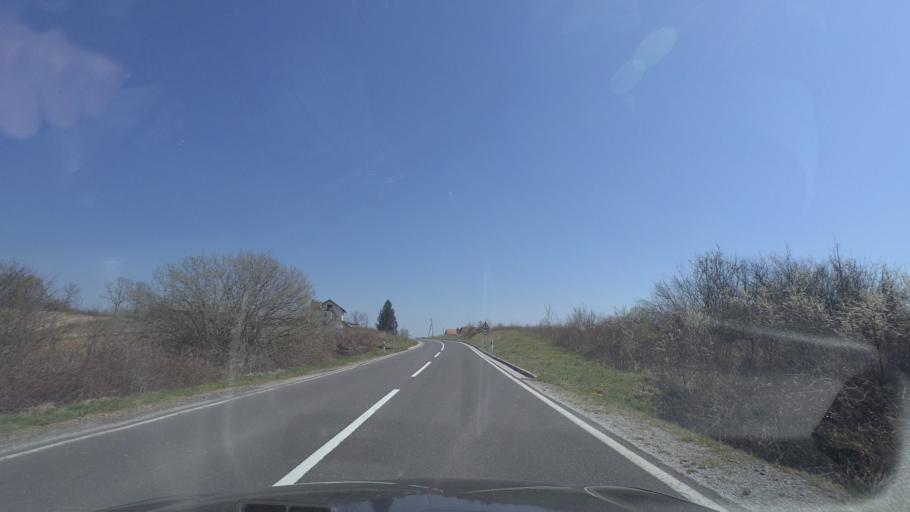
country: HR
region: Sisacko-Moslavacka
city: Gvozd
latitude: 45.3303
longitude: 15.9280
